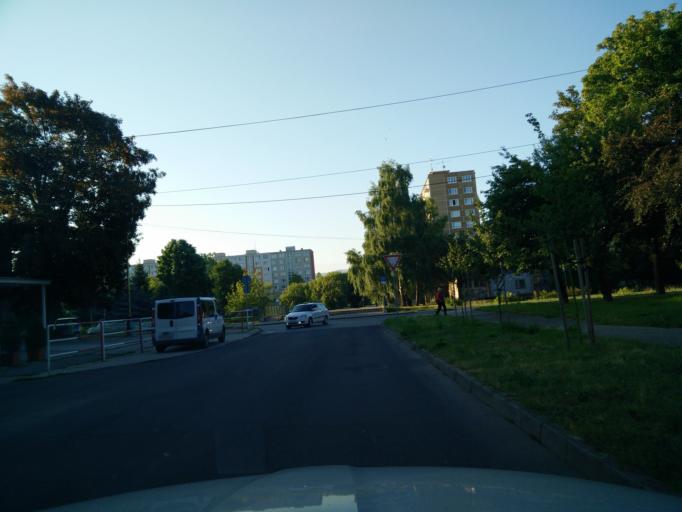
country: SK
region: Nitriansky
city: Bojnice
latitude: 48.7696
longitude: 18.6033
